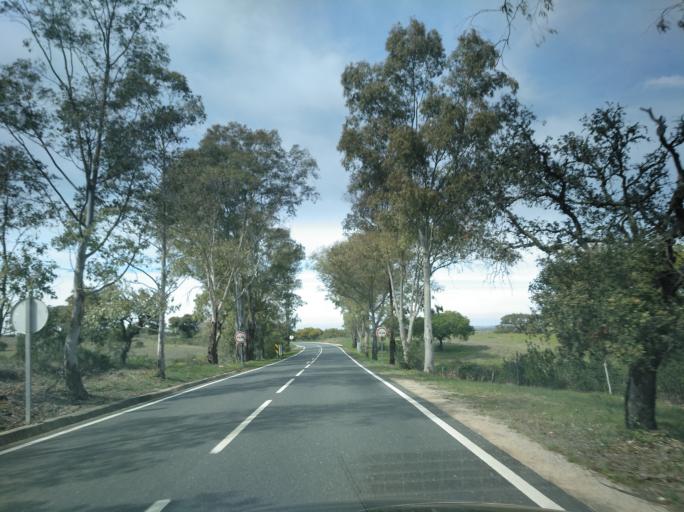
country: PT
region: Beja
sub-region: Mertola
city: Mertola
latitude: 37.7174
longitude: -7.7569
